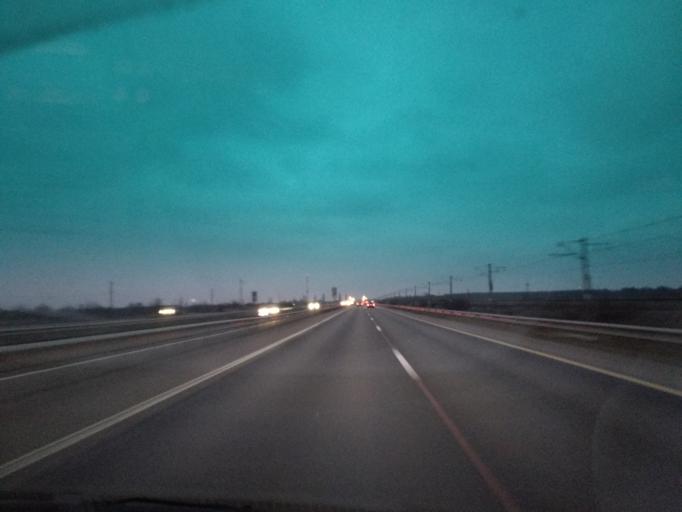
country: RU
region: Adygeya
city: Adygeysk
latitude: 44.8142
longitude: 39.2275
